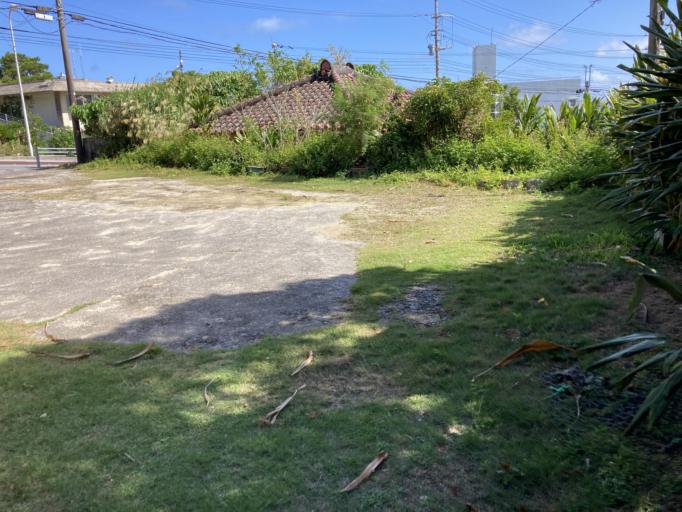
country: JP
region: Okinawa
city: Tomigusuku
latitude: 26.1453
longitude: 127.7918
